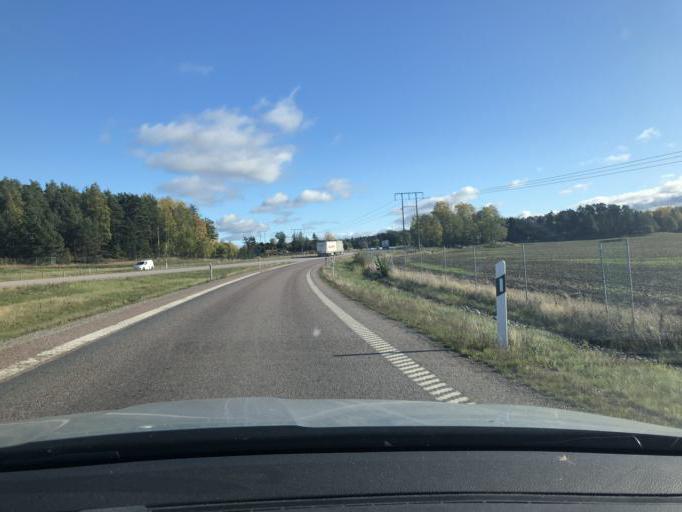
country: SE
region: Soedermanland
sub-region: Eskilstuna Kommun
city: Eskilstuna
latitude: 59.3774
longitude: 16.5934
